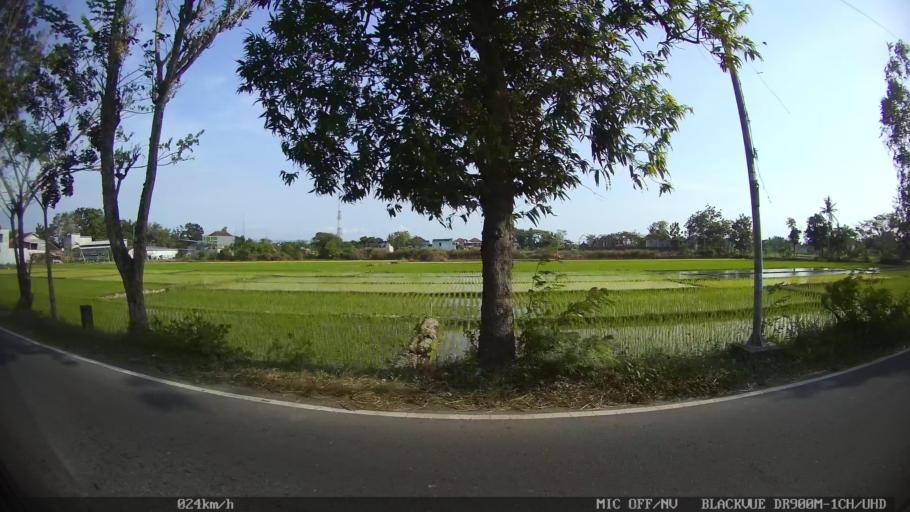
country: ID
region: Daerah Istimewa Yogyakarta
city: Bantul
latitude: -7.8786
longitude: 110.3298
